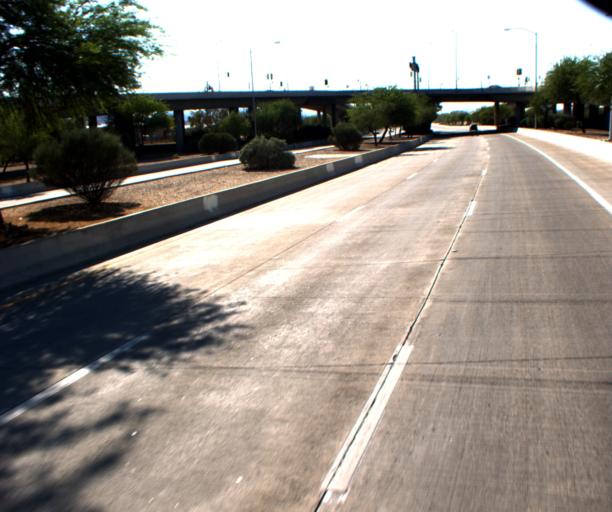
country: US
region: Arizona
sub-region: Pima County
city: Tucson
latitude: 32.2111
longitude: -110.9474
